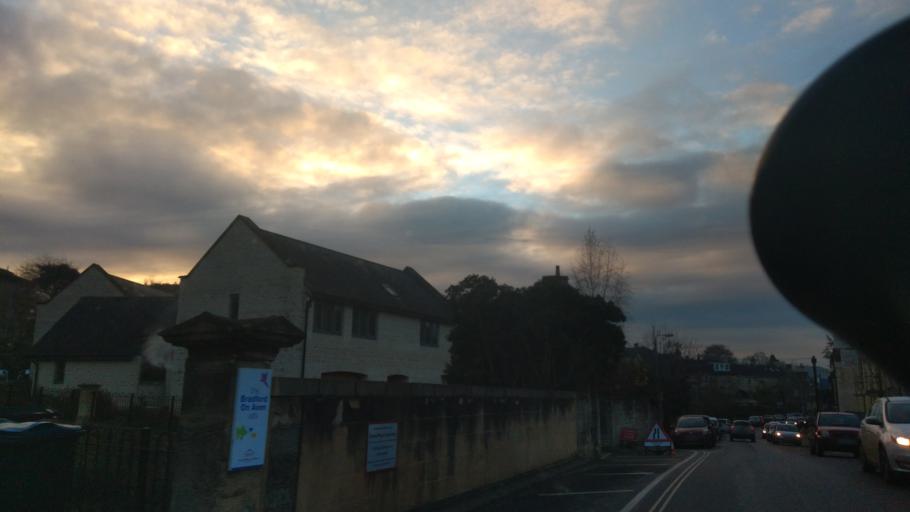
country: GB
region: England
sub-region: Wiltshire
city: Bradford-on-Avon
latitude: 51.3450
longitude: -2.2518
